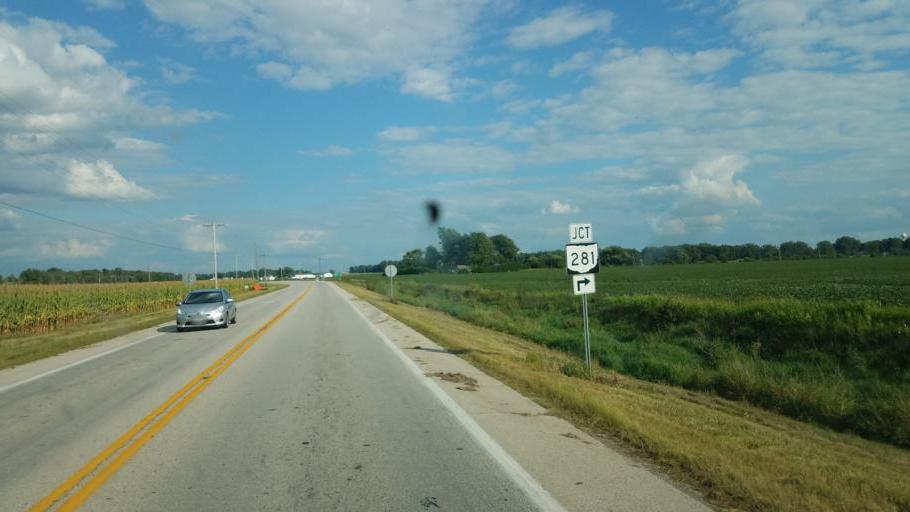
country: US
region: Ohio
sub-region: Wood County
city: Pemberville
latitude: 41.3426
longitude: -83.4406
